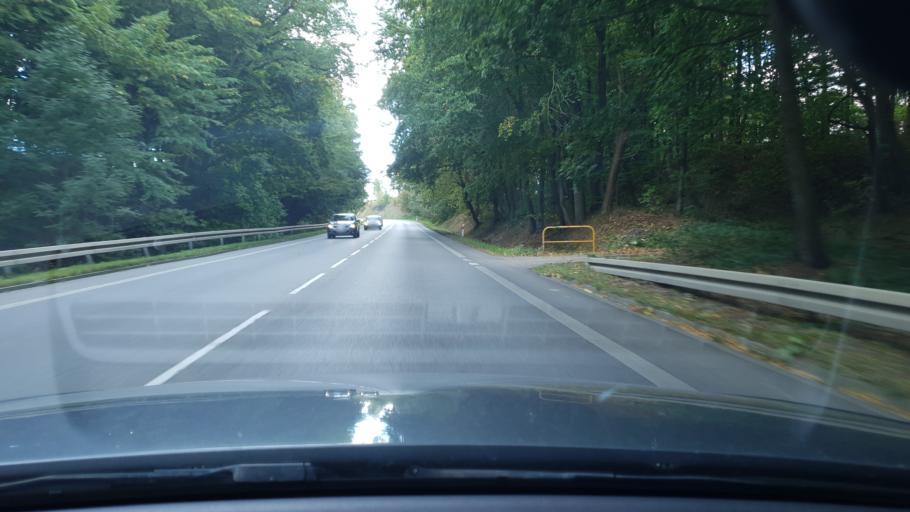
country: PL
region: Pomeranian Voivodeship
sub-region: Powiat wejherowski
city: Rekowo Dolne
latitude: 54.6599
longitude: 18.3619
